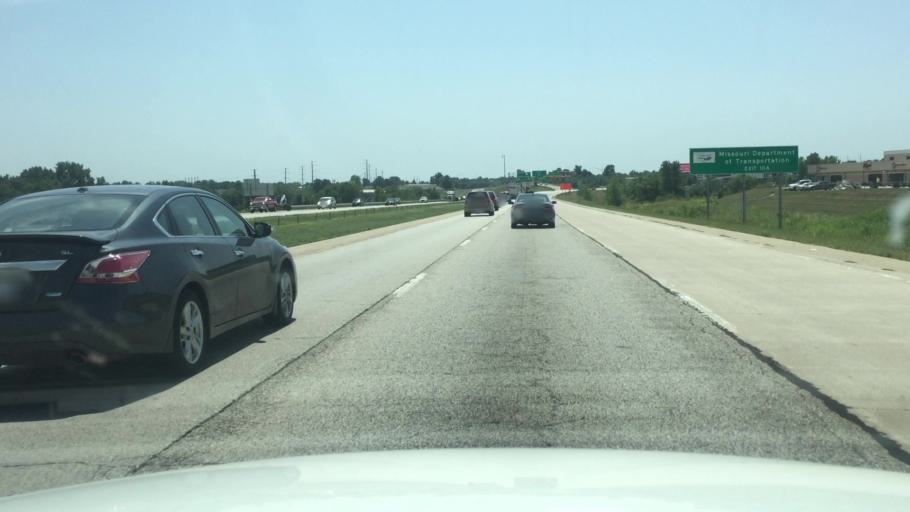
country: US
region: Missouri
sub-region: Jackson County
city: Lees Summit
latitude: 38.9554
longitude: -94.3604
